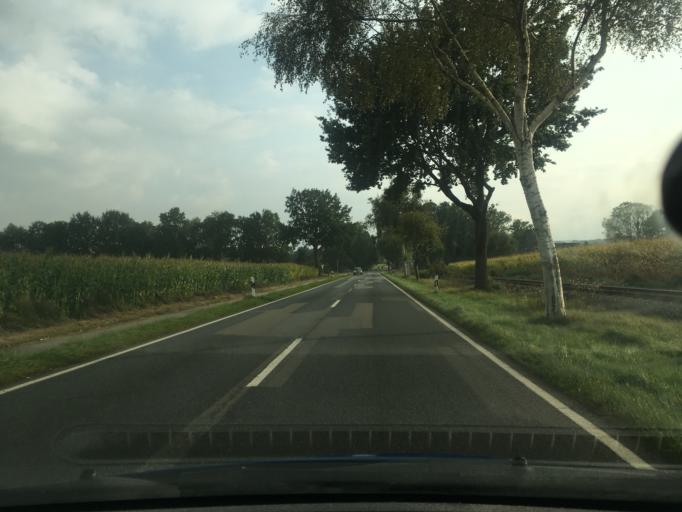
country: DE
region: Lower Saxony
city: Salzhausen
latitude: 53.2179
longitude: 10.1650
